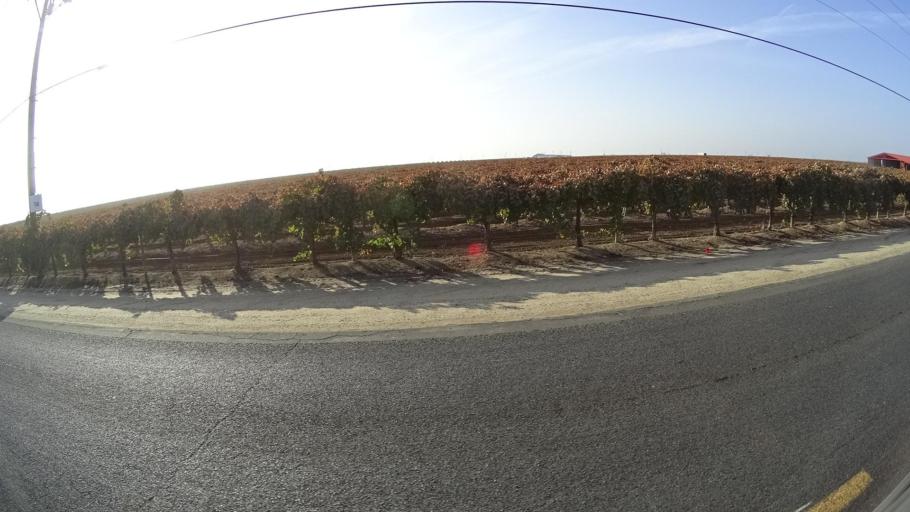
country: US
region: California
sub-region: Kern County
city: McFarland
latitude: 35.6746
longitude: -119.1895
